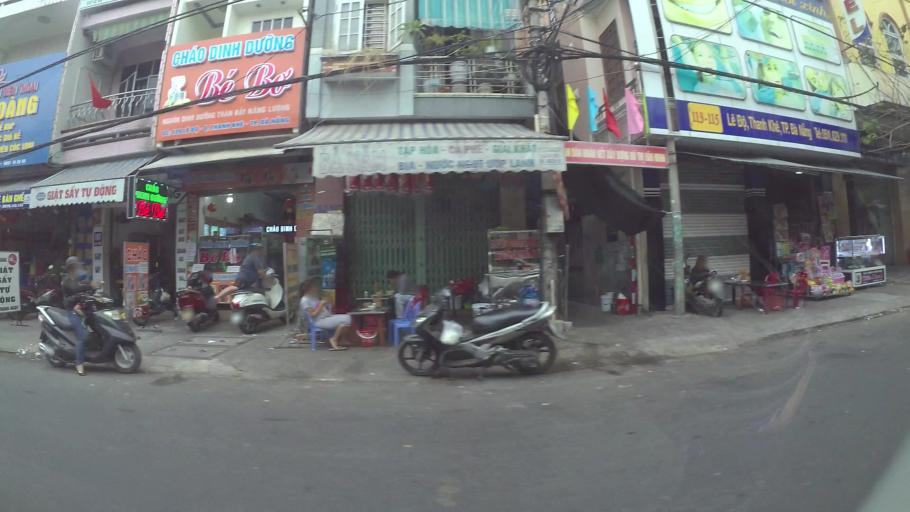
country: VN
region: Da Nang
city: Thanh Khe
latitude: 16.0676
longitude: 108.2015
